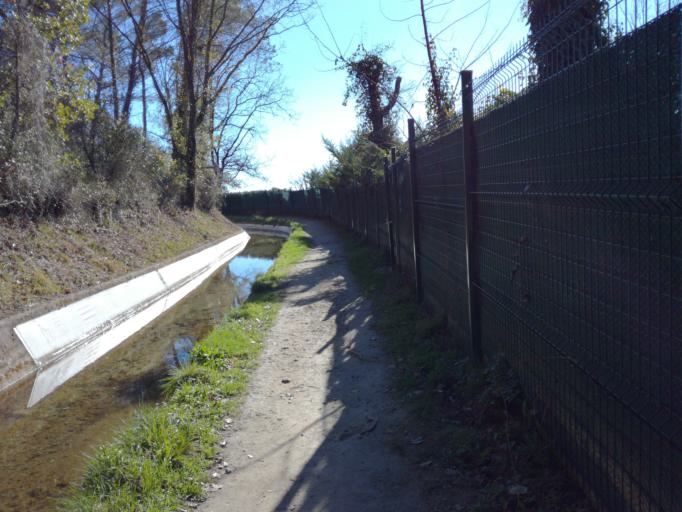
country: FR
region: Provence-Alpes-Cote d'Azur
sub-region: Departement des Alpes-Maritimes
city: Mouans-Sartoux
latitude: 43.6275
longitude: 6.9796
